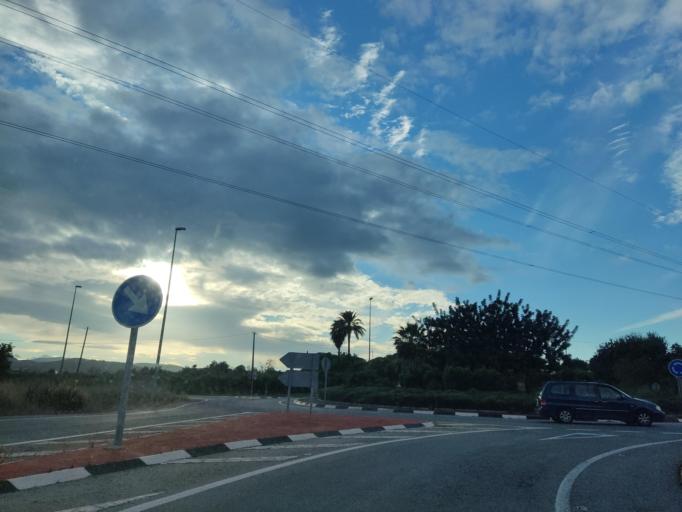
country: ES
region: Valencia
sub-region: Provincia de Alicante
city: Pedreguer
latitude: 38.8071
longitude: 0.0343
